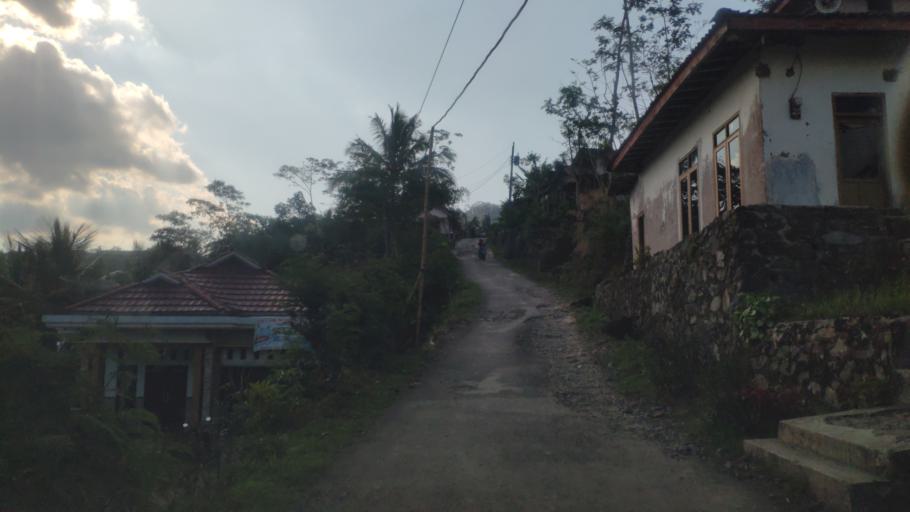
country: ID
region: Central Java
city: Buaran
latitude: -7.2353
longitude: 109.5722
